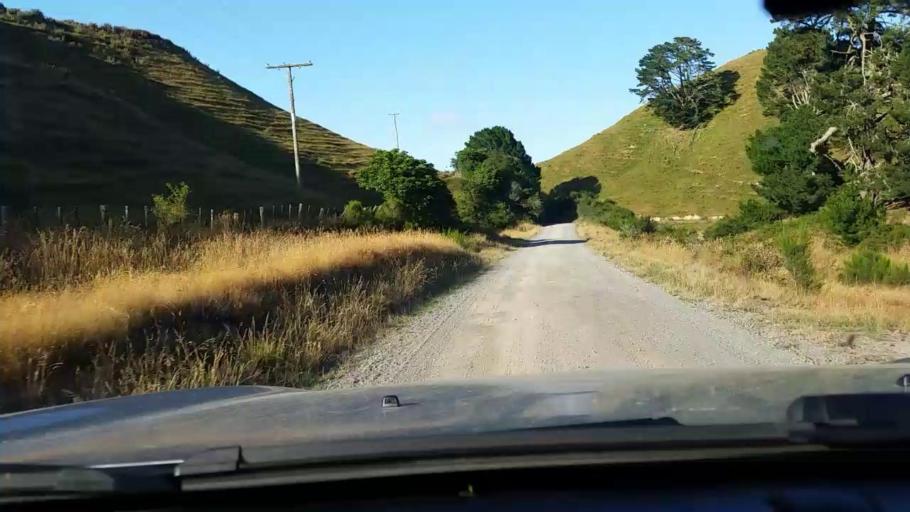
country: NZ
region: Waikato
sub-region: Taupo District
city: Taupo
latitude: -38.4777
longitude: 176.2182
